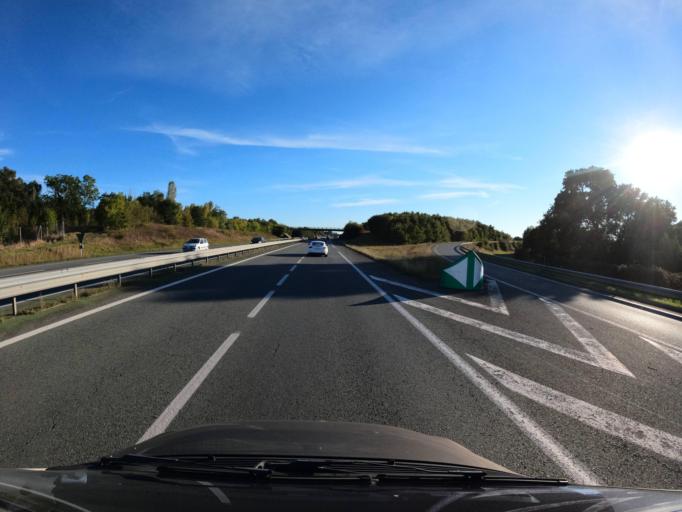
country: FR
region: Pays de la Loire
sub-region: Departement de Maine-et-Loire
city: Nuaille
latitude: 47.0882
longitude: -0.8240
